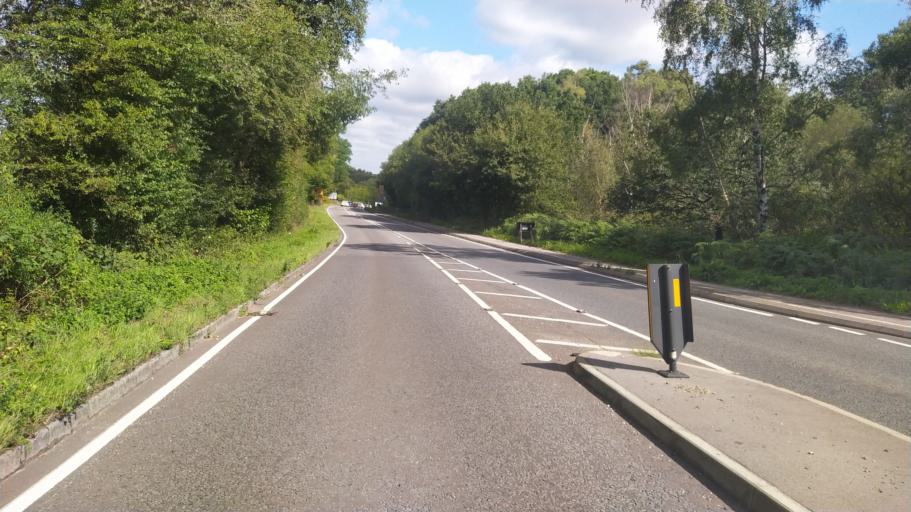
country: GB
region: England
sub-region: Hampshire
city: Lindford
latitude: 51.1352
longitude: -0.8548
